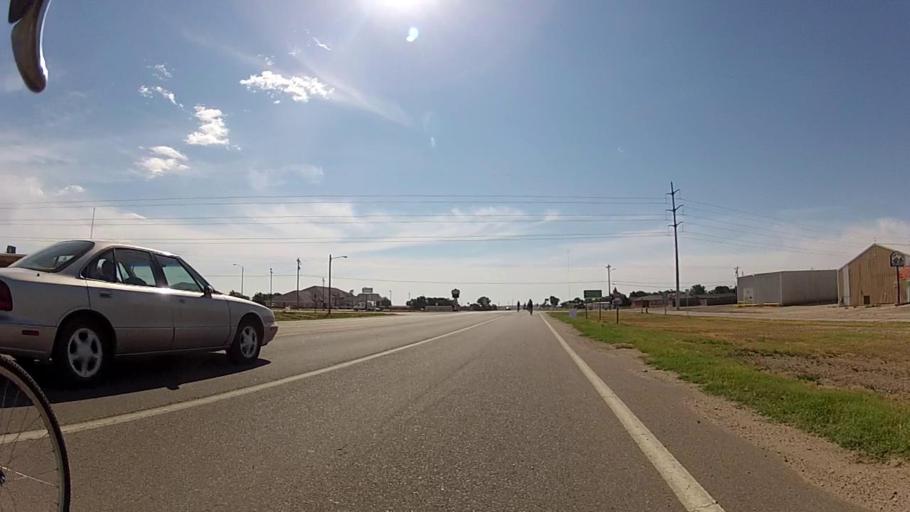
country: US
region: Kansas
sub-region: Grant County
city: Ulysses
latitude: 37.5754
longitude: -101.3462
